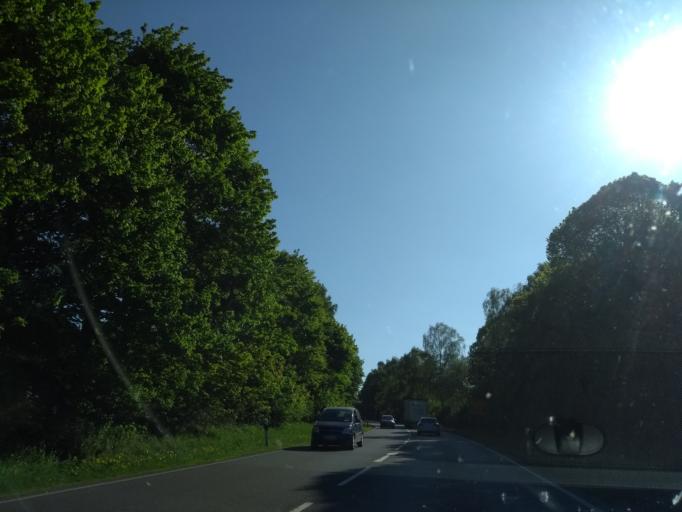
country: DE
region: Hesse
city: Battenberg
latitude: 51.0122
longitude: 8.6547
